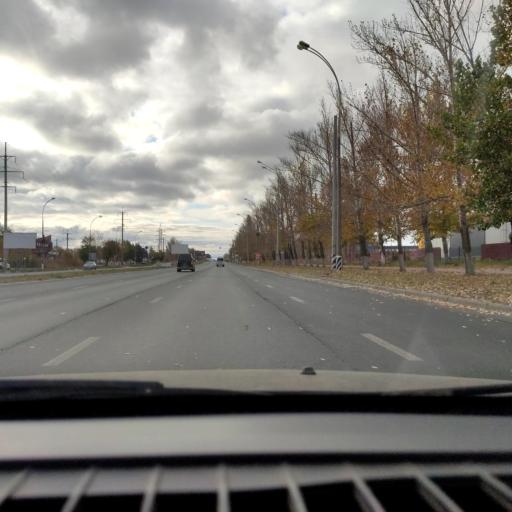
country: RU
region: Samara
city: Tol'yatti
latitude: 53.5490
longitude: 49.2864
